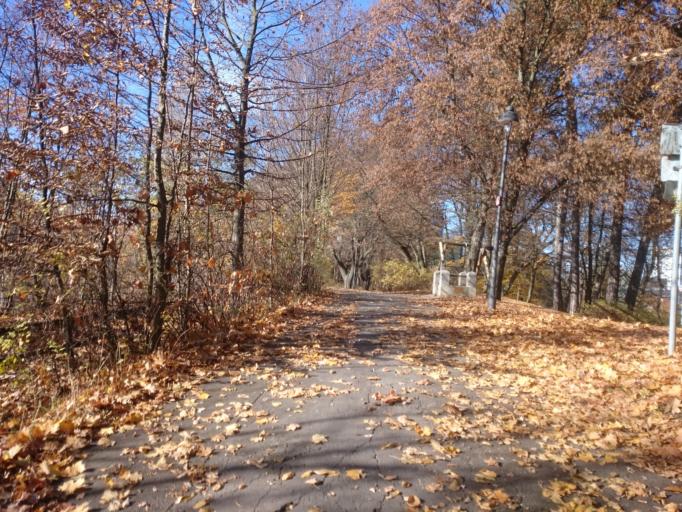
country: DE
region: Bavaria
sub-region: Upper Franconia
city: Hof
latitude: 50.3230
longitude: 11.9024
